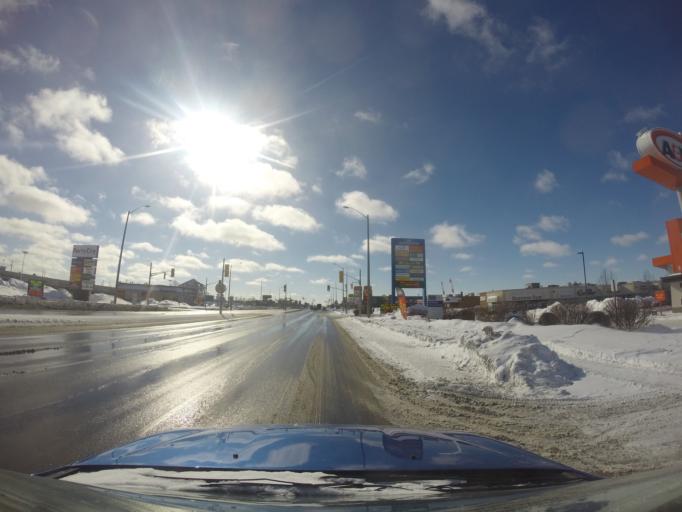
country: CA
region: Ontario
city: Cambridge
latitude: 43.4035
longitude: -80.3267
